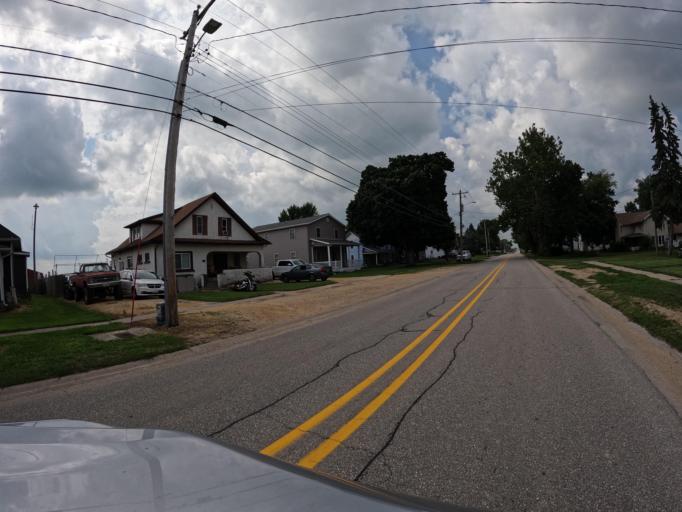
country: US
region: Iowa
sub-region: Clinton County
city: Camanche
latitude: 41.7989
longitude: -90.3549
